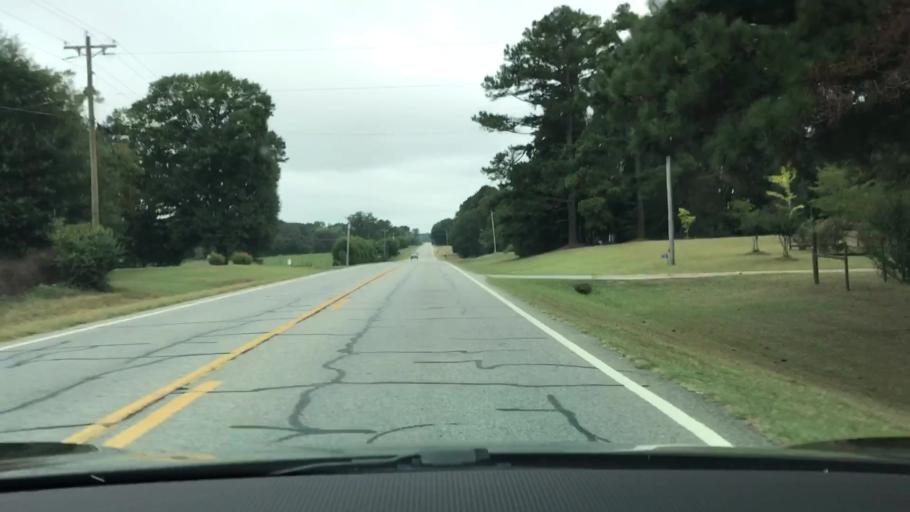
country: US
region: Georgia
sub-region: Oconee County
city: Watkinsville
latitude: 33.7957
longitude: -83.3297
